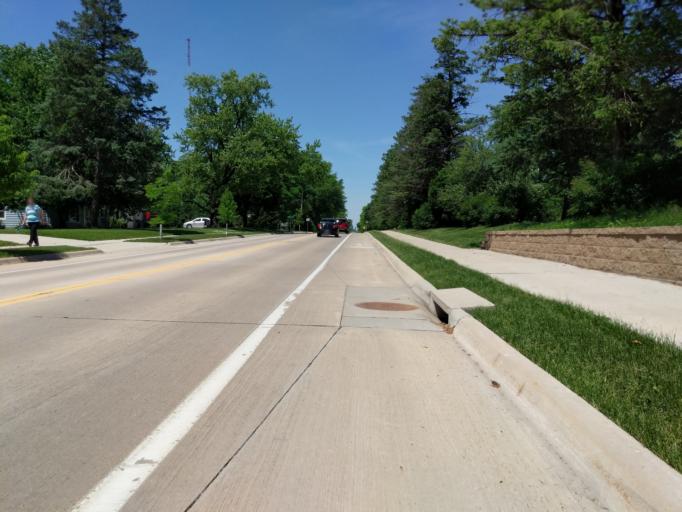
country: US
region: Iowa
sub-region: Linn County
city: Cedar Rapids
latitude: 42.0229
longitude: -91.6385
